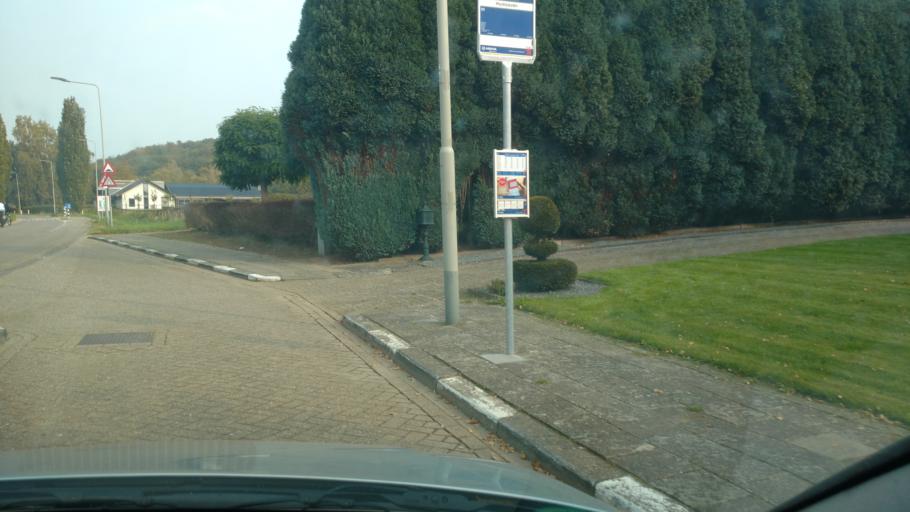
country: NL
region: Limburg
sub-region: Gemeente Meerssen
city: Meerssen
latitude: 50.8928
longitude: 5.7630
